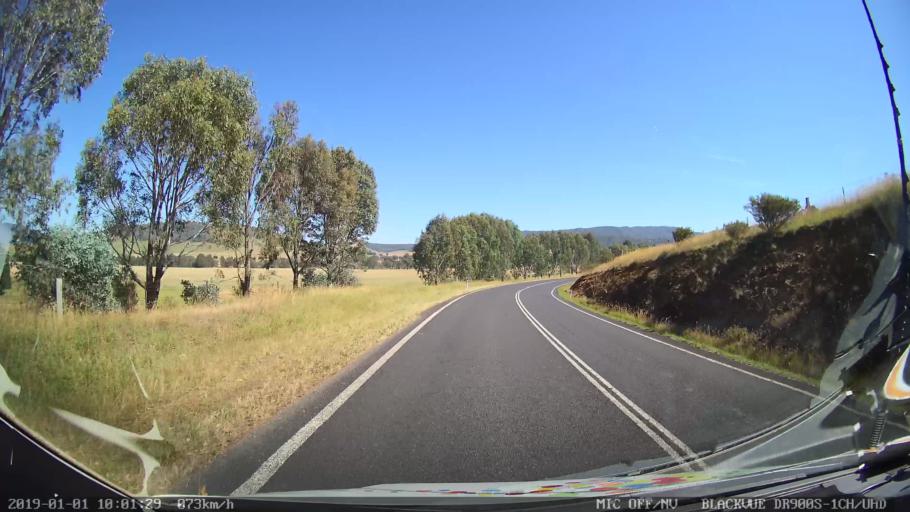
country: AU
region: New South Wales
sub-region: Snowy River
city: Jindabyne
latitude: -36.1911
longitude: 148.1007
